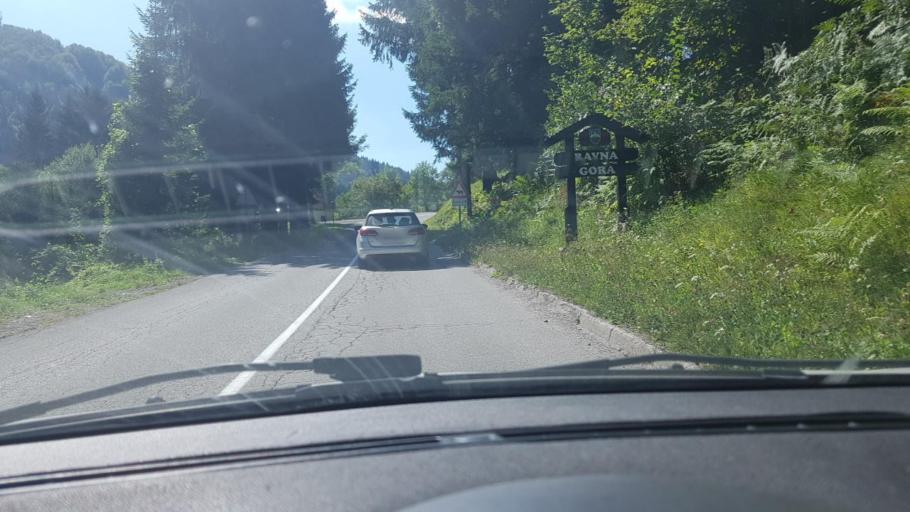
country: HR
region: Primorsko-Goranska
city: Vrbovsko
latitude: 45.3795
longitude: 14.9685
